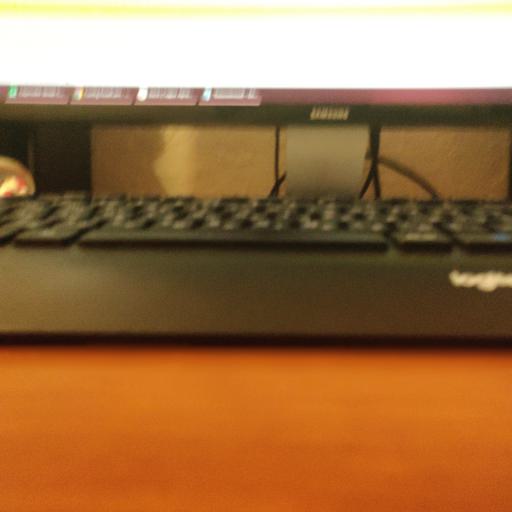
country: PL
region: Lodz Voivodeship
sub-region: Powiat tomaszowski
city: Lubochnia
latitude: 51.6554
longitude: 20.0280
